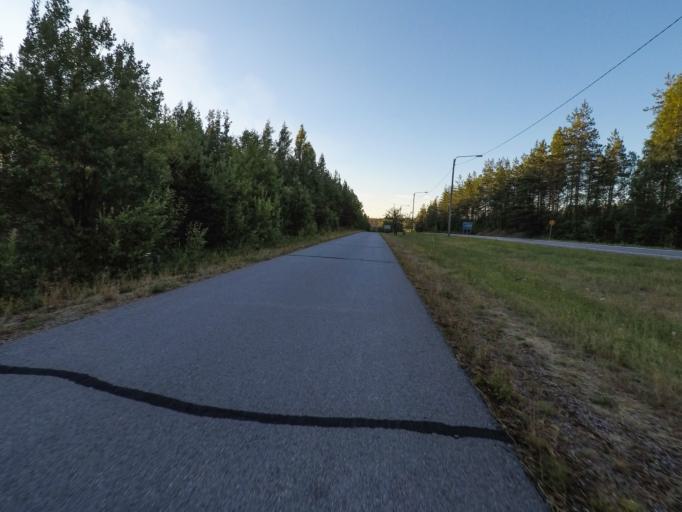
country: FI
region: South Karelia
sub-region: Imatra
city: Ruokolahti
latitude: 61.2566
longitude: 28.8789
